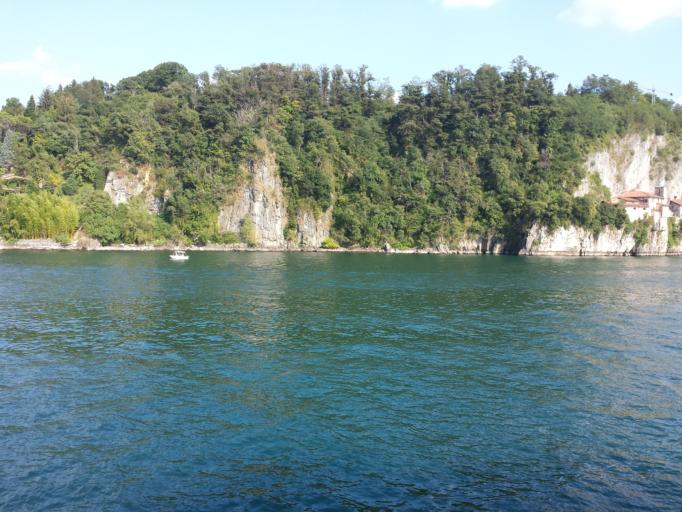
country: IT
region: Lombardy
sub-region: Provincia di Varese
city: Leggiuno
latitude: 45.8792
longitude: 8.5940
